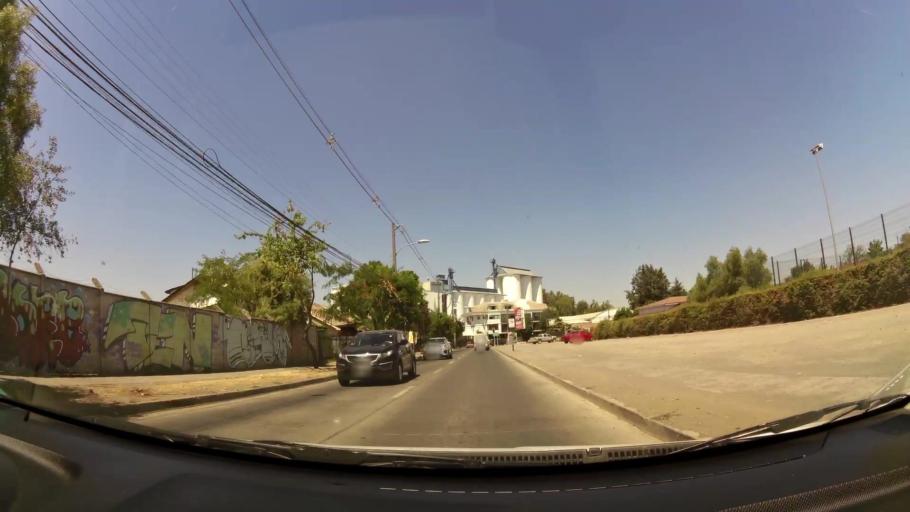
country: CL
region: Maule
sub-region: Provincia de Curico
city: Curico
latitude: -34.9825
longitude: -71.2176
